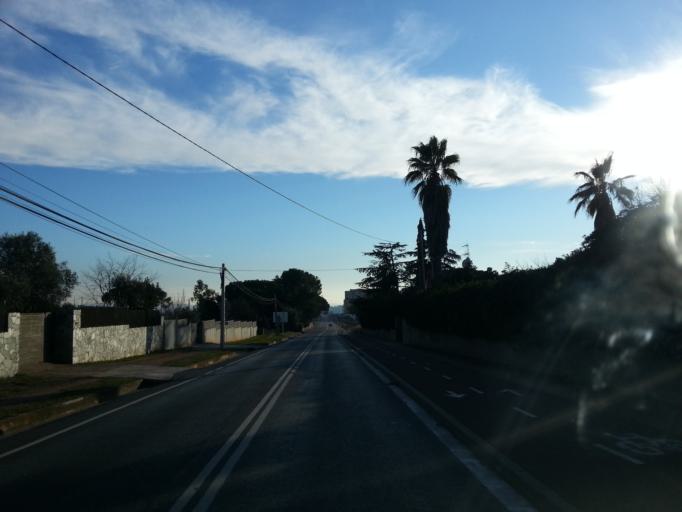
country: ES
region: Catalonia
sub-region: Provincia de Barcelona
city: Matadepera
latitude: 41.5900
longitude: 2.0192
